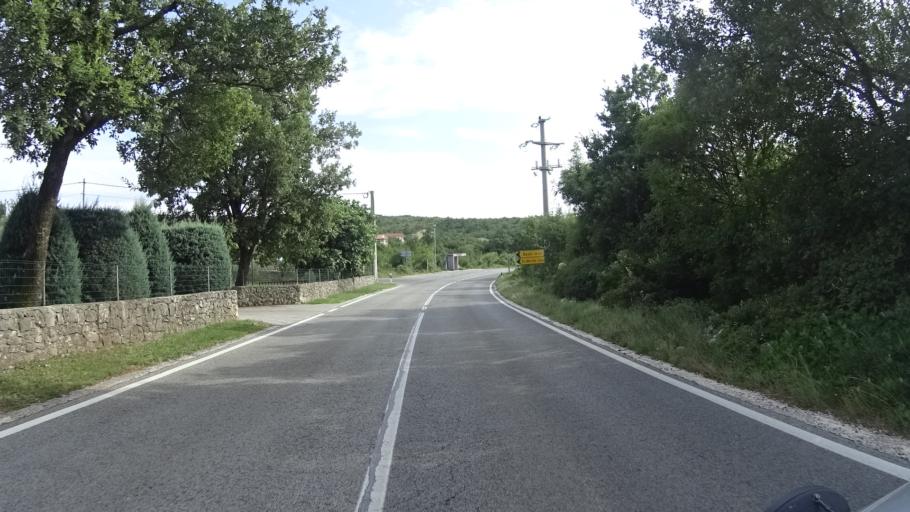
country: HR
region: Istarska
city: Rasa
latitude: 45.0560
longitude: 14.0890
